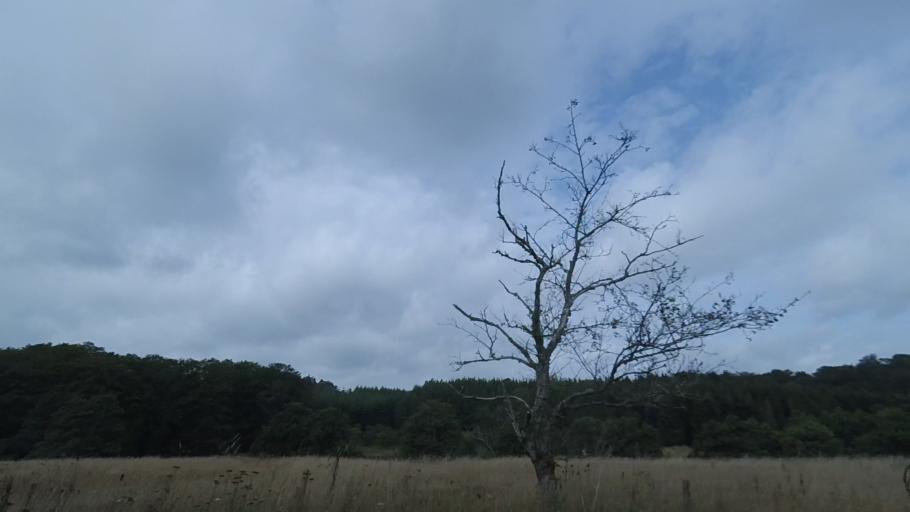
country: DK
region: Central Jutland
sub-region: Syddjurs Kommune
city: Ryomgard
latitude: 56.3985
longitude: 10.4897
